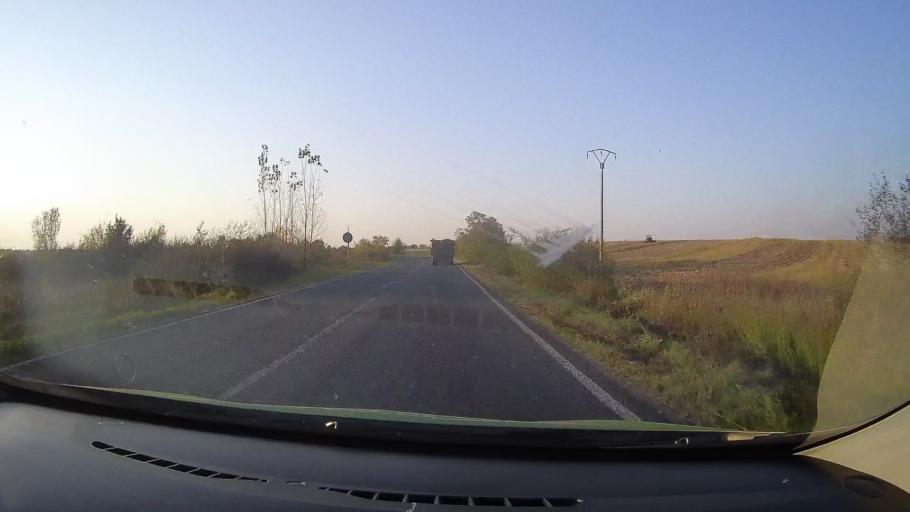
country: RO
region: Arad
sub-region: Comuna Barsa
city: Barsa
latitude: 46.3893
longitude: 22.0628
